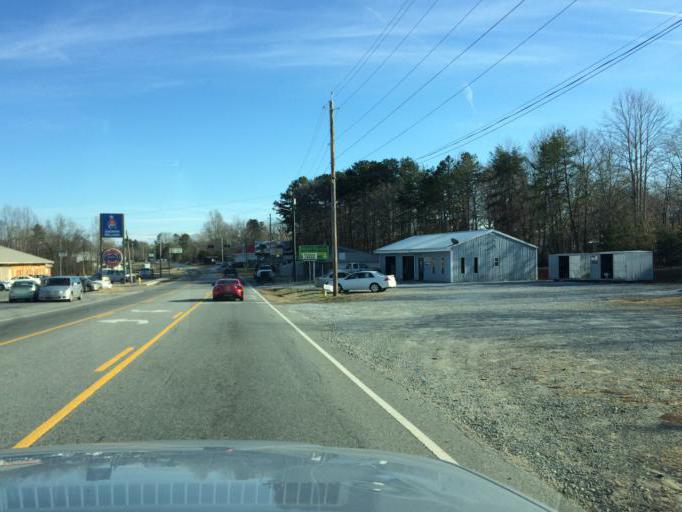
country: US
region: North Carolina
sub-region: Rutherford County
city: Forest City
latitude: 35.3426
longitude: -81.8816
